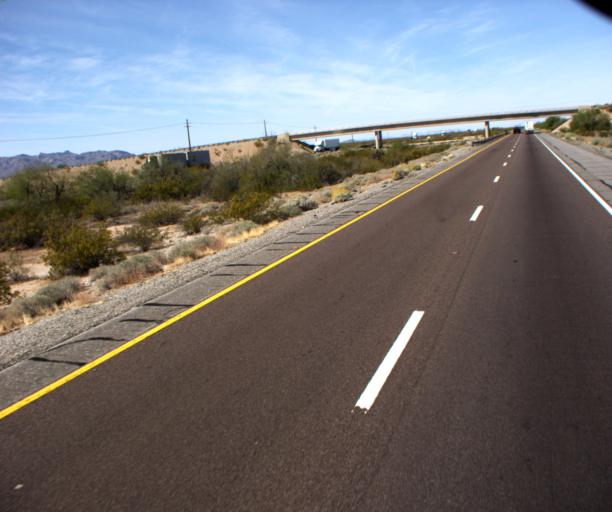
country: US
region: Arizona
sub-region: La Paz County
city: Salome
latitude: 33.5610
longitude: -113.2980
